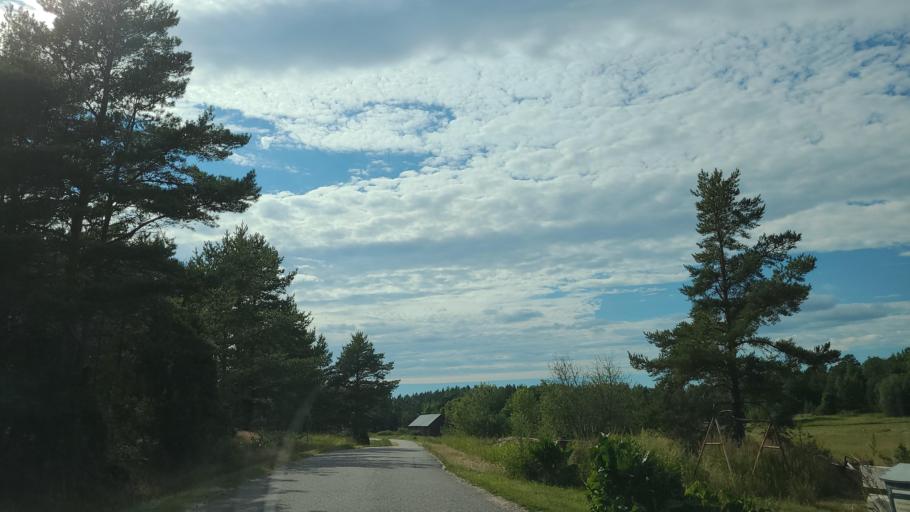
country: FI
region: Varsinais-Suomi
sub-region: Turku
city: Rymaettylae
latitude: 60.2901
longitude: 21.9598
